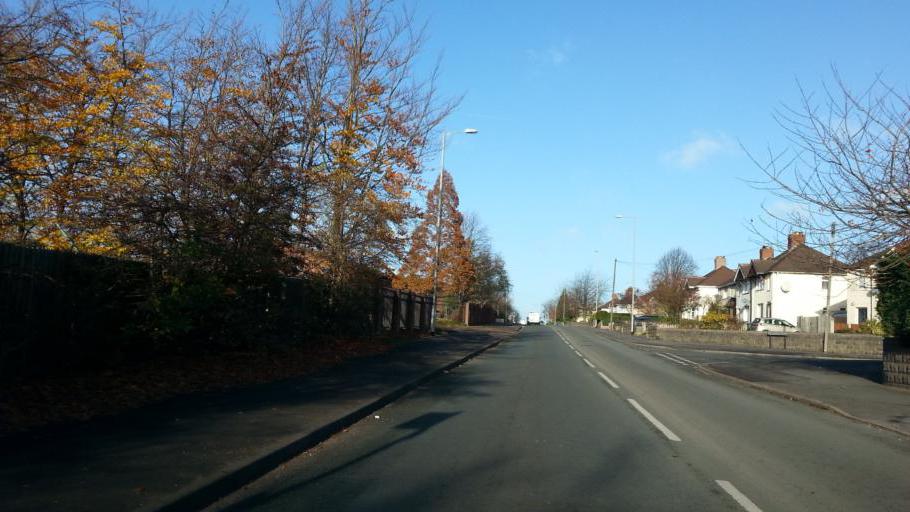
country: GB
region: England
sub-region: Staffordshire
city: Cannock
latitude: 52.6793
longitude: -2.0336
